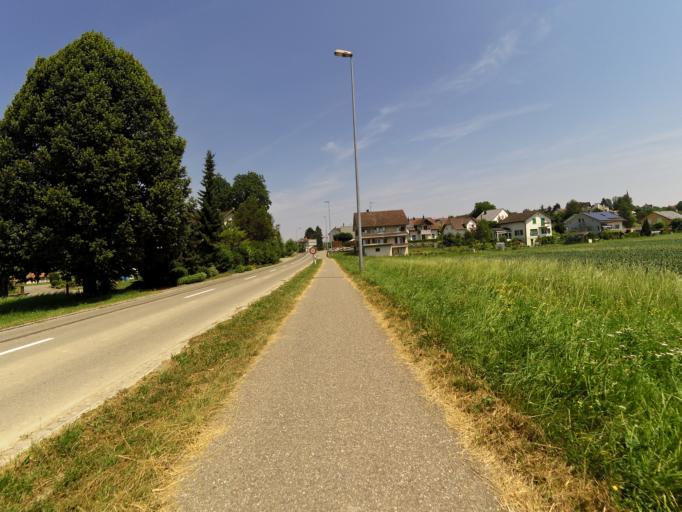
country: CH
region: Thurgau
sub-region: Weinfelden District
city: Wigoltingen
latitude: 47.5952
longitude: 9.0239
